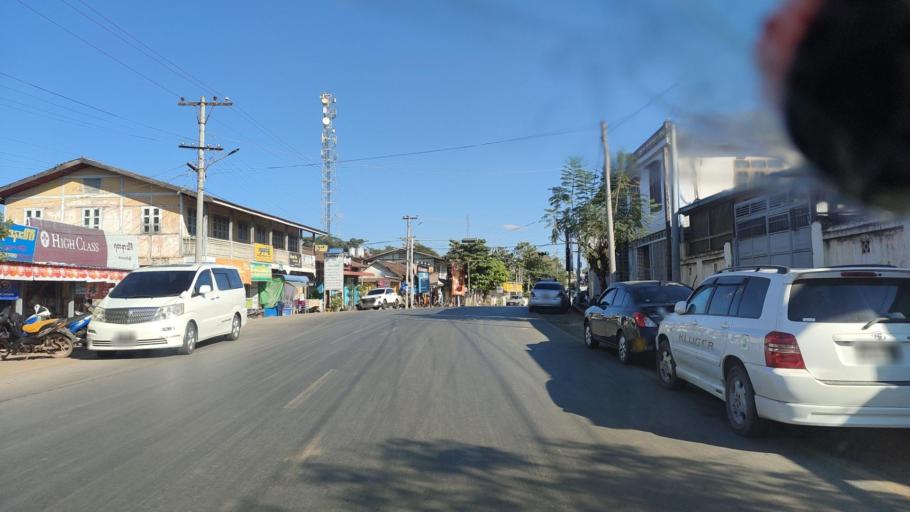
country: MM
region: Mandalay
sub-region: Pyin Oo Lwin District
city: Pyin Oo Lwin
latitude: 22.3312
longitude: 96.8001
